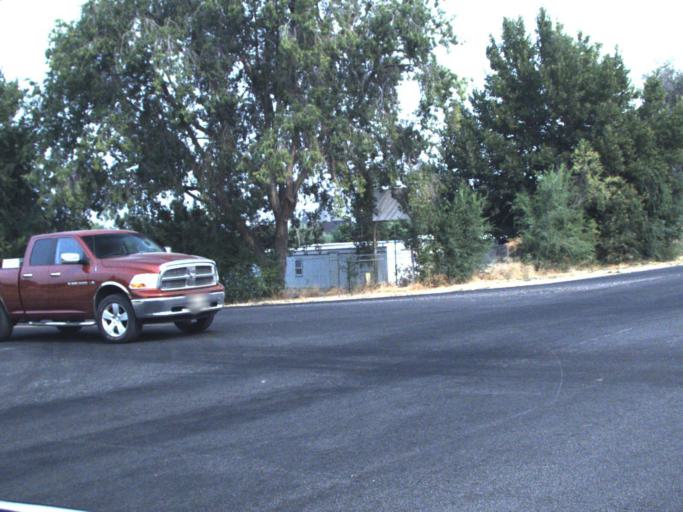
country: US
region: Washington
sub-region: Yakima County
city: Granger
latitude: 46.3396
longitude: -120.1870
